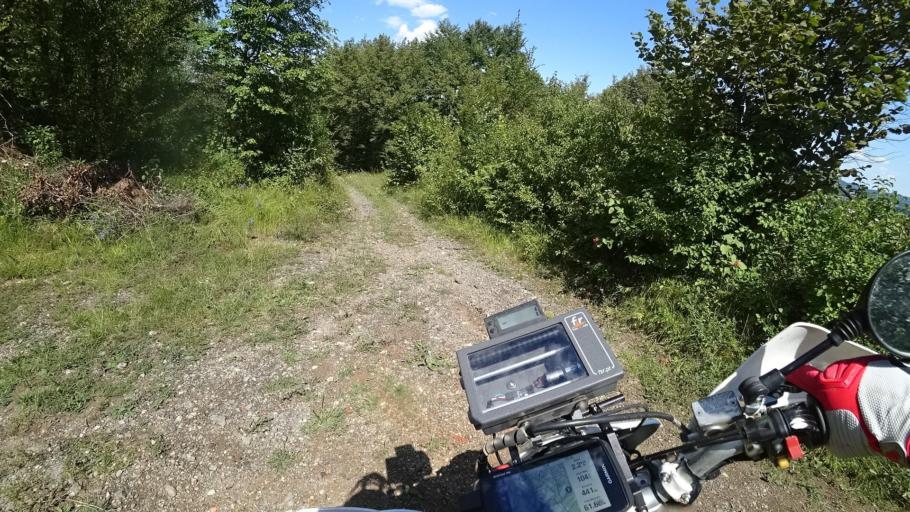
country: HR
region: Karlovacka
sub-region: Grad Ogulin
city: Ogulin
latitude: 45.2498
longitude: 15.2158
